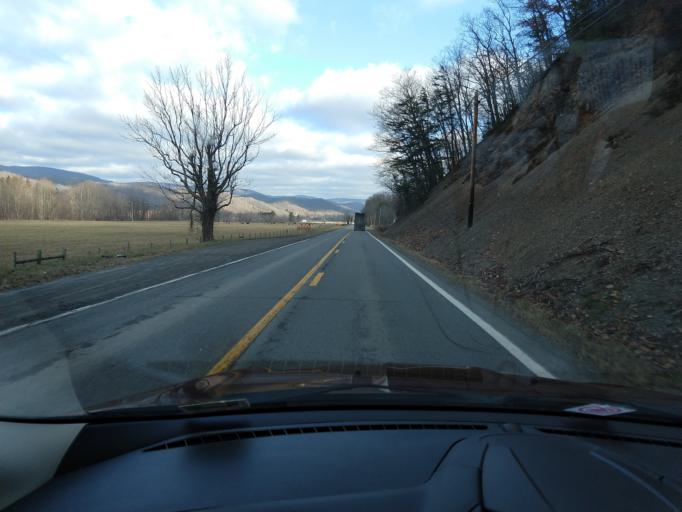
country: US
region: West Virginia
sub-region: Randolph County
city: Elkins
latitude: 38.6854
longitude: -79.9740
